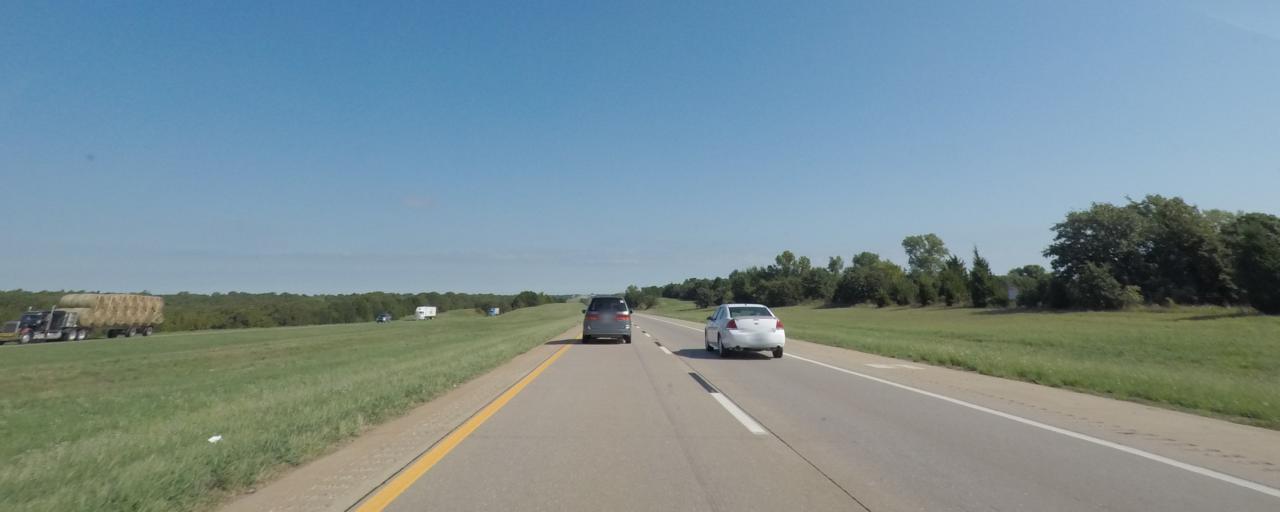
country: US
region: Oklahoma
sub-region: Logan County
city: Guthrie
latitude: 35.7683
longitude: -97.4159
